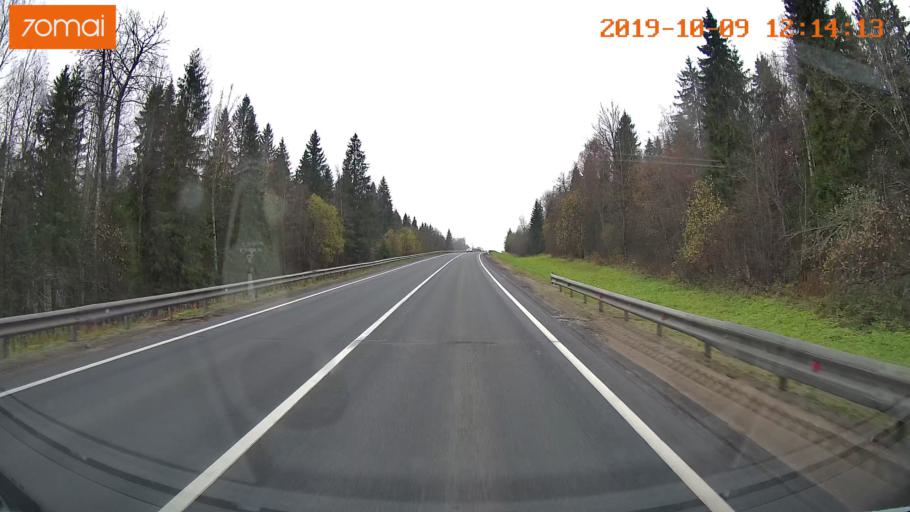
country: RU
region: Jaroslavl
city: Prechistoye
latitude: 58.4990
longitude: 40.3395
